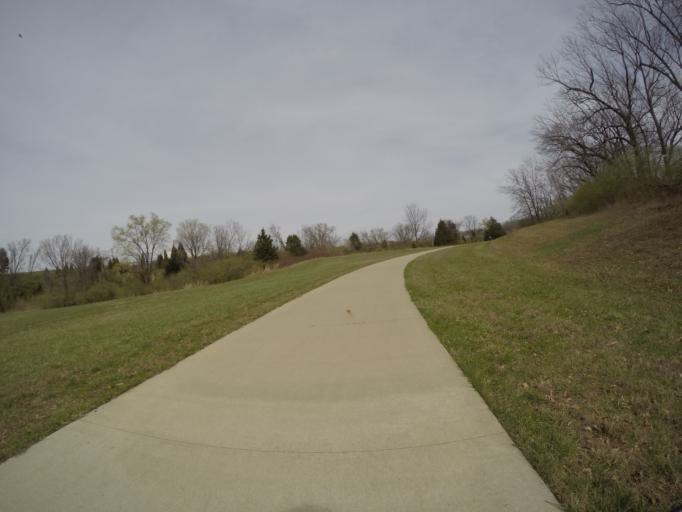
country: US
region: Kansas
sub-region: Johnson County
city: Leawood
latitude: 38.9386
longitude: -94.5653
